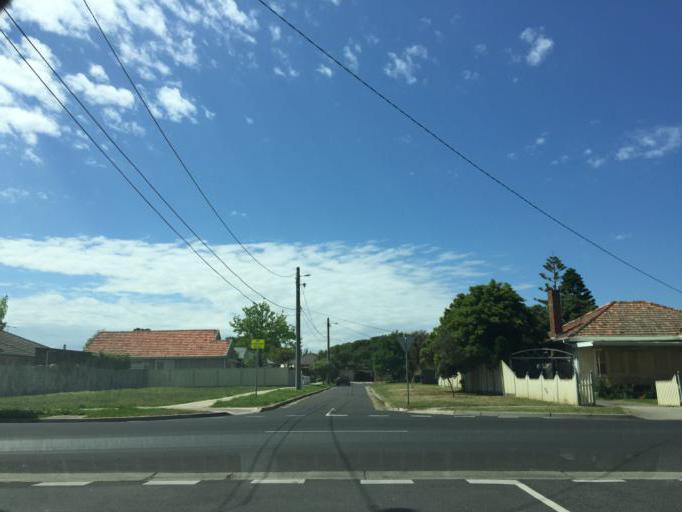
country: AU
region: Victoria
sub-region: Maribyrnong
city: Braybrook
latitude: -37.7876
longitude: 144.8409
